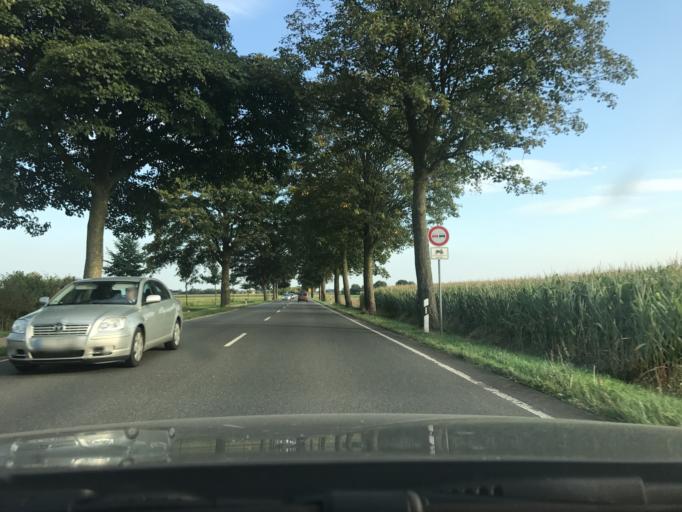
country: DE
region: North Rhine-Westphalia
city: Geldern
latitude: 51.4712
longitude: 6.3539
